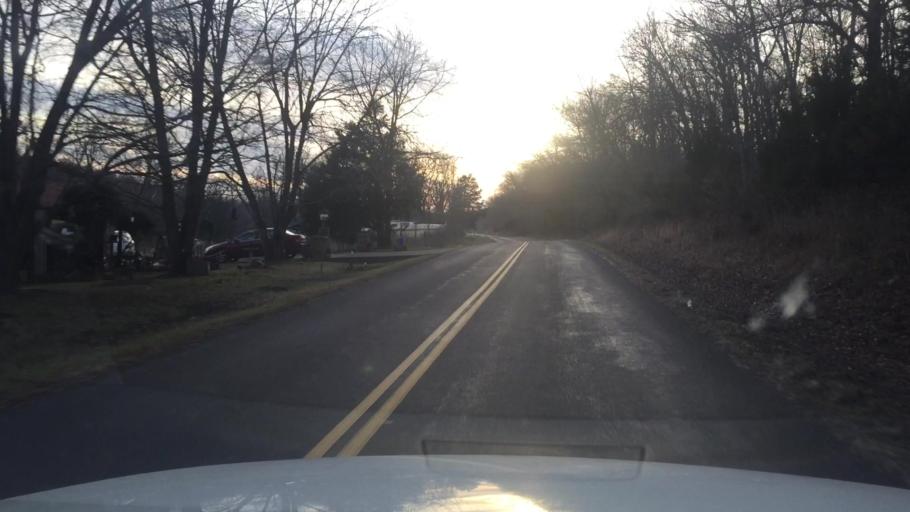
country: US
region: Missouri
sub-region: Miller County
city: Eldon
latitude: 38.3531
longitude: -92.6961
